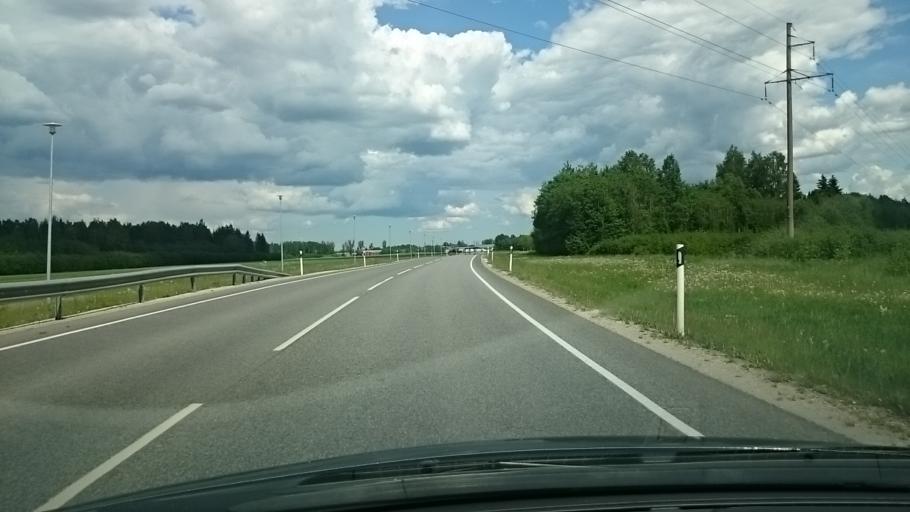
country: EE
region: Jaervamaa
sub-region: Paide linn
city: Paide
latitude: 58.8729
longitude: 25.4968
